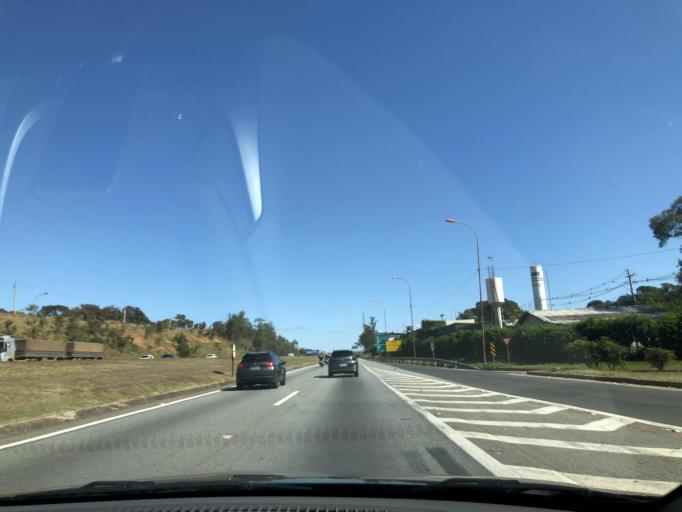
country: BR
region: Sao Paulo
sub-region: Sorocaba
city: Sorocaba
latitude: -23.4348
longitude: -47.3730
